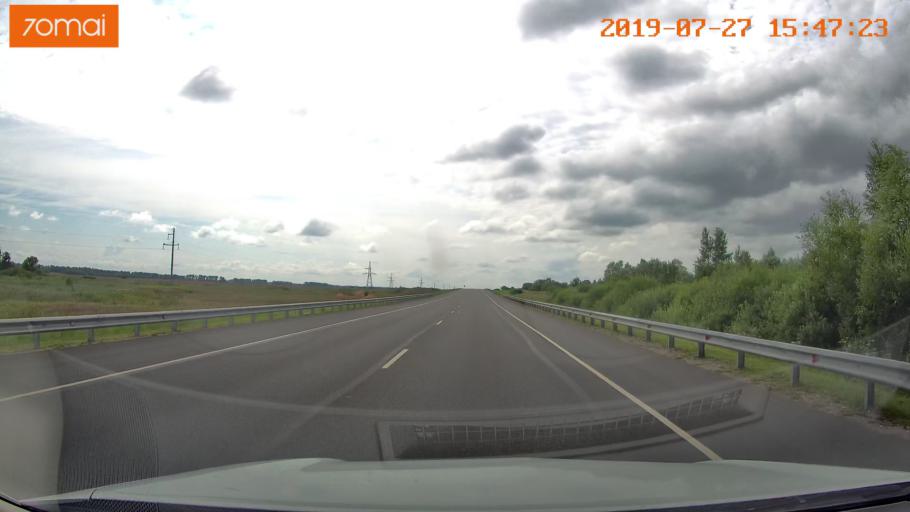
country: RU
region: Kaliningrad
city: Gusev
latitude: 54.6019
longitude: 22.0891
